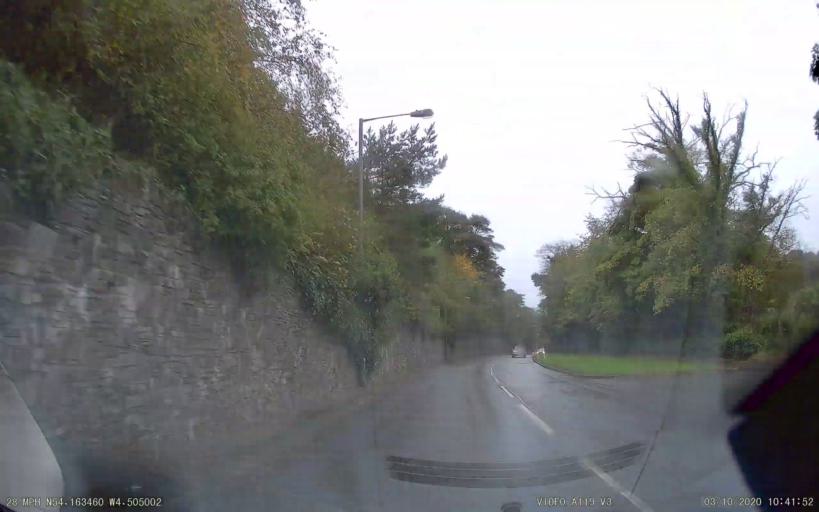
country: IM
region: Douglas
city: Douglas
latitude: 54.1635
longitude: -4.5050
